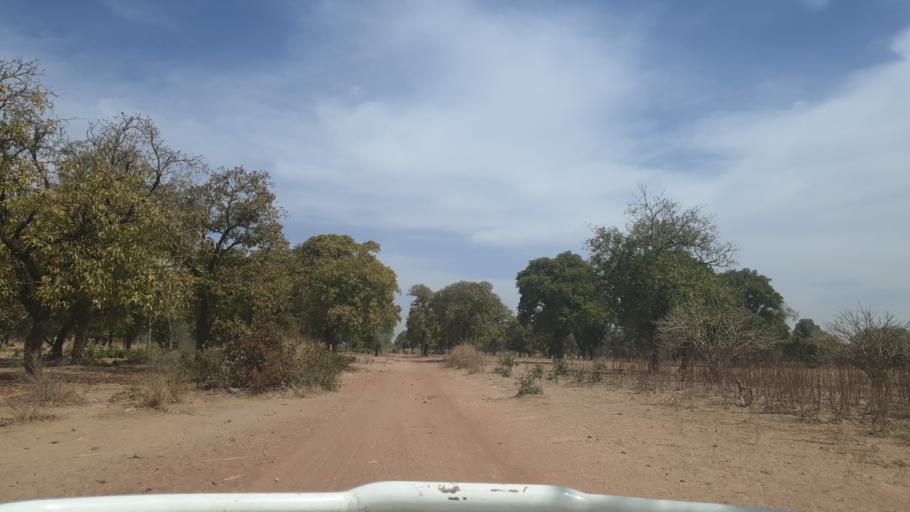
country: ML
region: Sikasso
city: Yorosso
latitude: 12.2743
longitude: -4.6916
